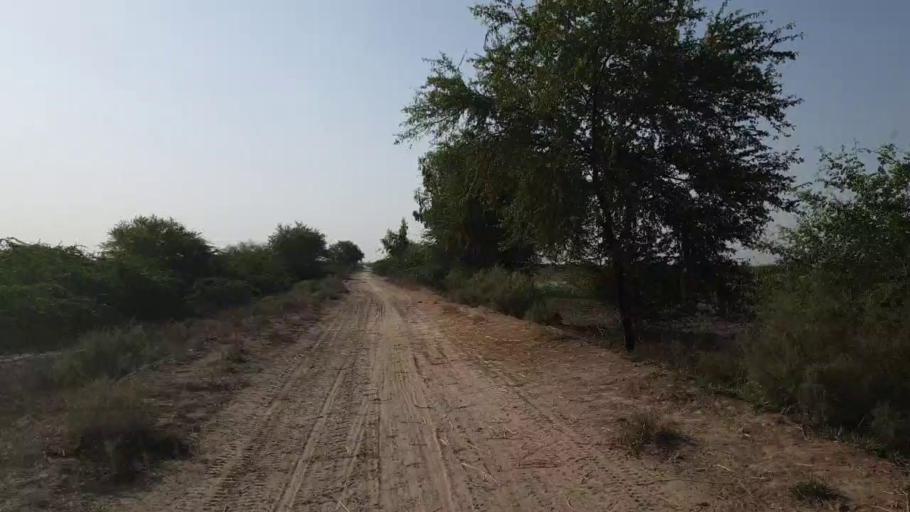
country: PK
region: Sindh
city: Kadhan
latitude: 24.6164
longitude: 69.0730
